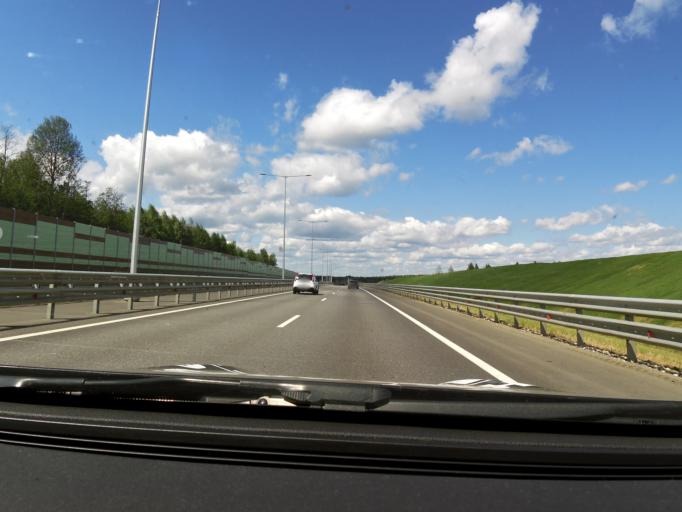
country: RU
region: Tverskaya
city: Vydropuzhsk
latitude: 57.3670
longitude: 34.6597
